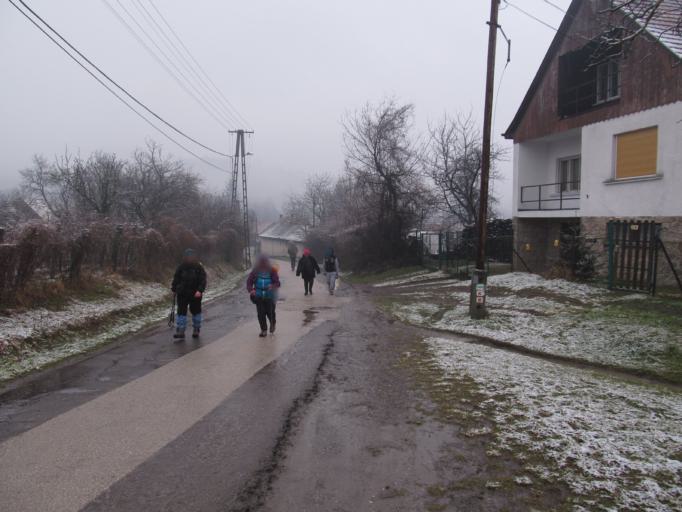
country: HU
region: Nograd
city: Diosjeno
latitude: 47.9451
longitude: 19.0331
